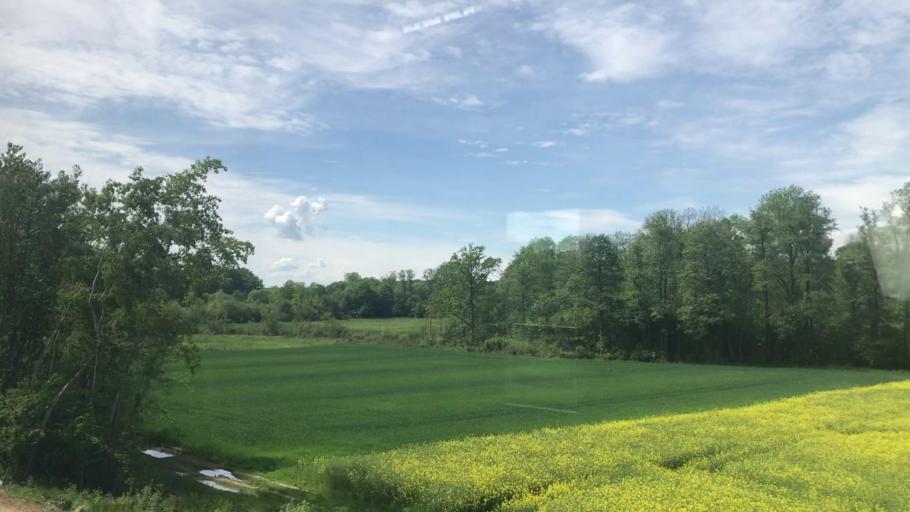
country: PL
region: Lower Silesian Voivodeship
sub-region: Powiat wroclawski
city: Sobotka
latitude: 50.9799
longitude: 16.6406
